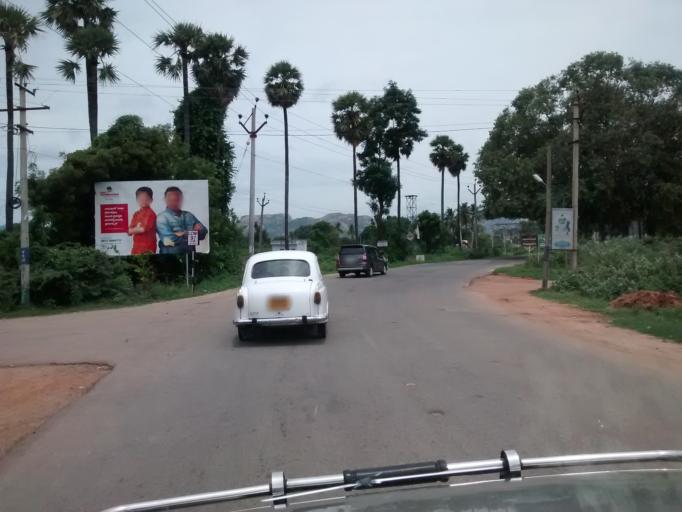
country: IN
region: Andhra Pradesh
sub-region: Chittoor
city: Narasingapuram
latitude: 13.6100
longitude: 79.3489
